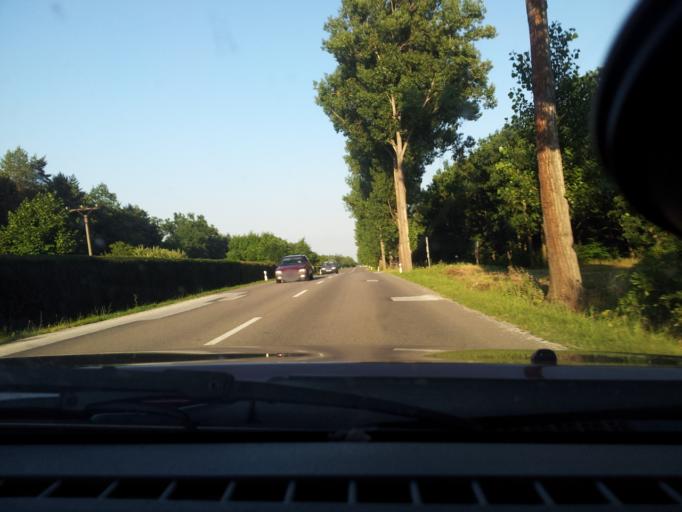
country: CZ
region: South Moravian
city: Dubnany
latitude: 48.8856
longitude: 17.0833
